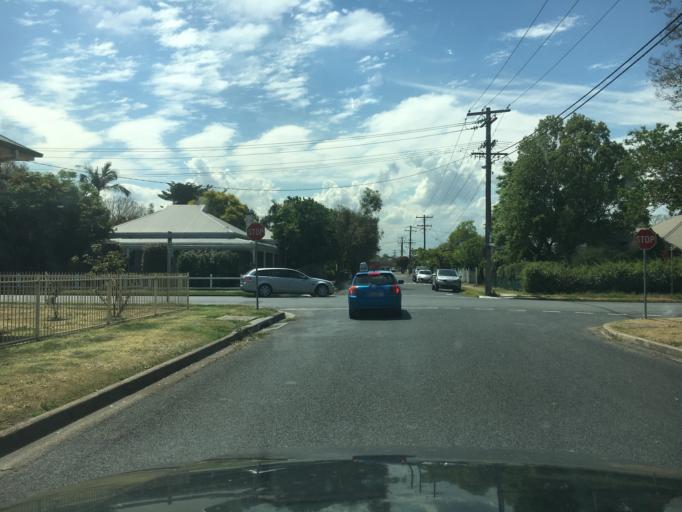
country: AU
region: New South Wales
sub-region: Singleton
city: Singleton
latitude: -32.5672
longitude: 151.1691
